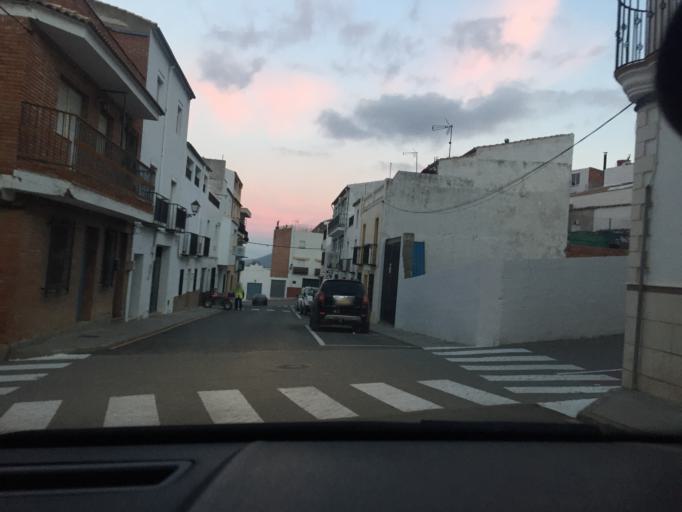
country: ES
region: Andalusia
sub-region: Provincia de Jaen
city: Torres
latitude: 37.7927
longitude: -3.4683
